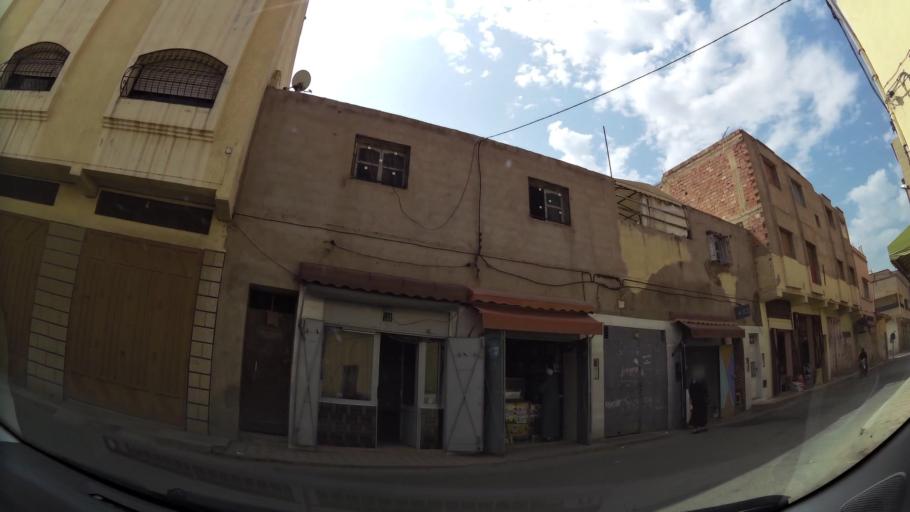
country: MA
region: Oriental
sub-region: Oujda-Angad
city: Oujda
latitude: 34.6825
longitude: -1.9058
